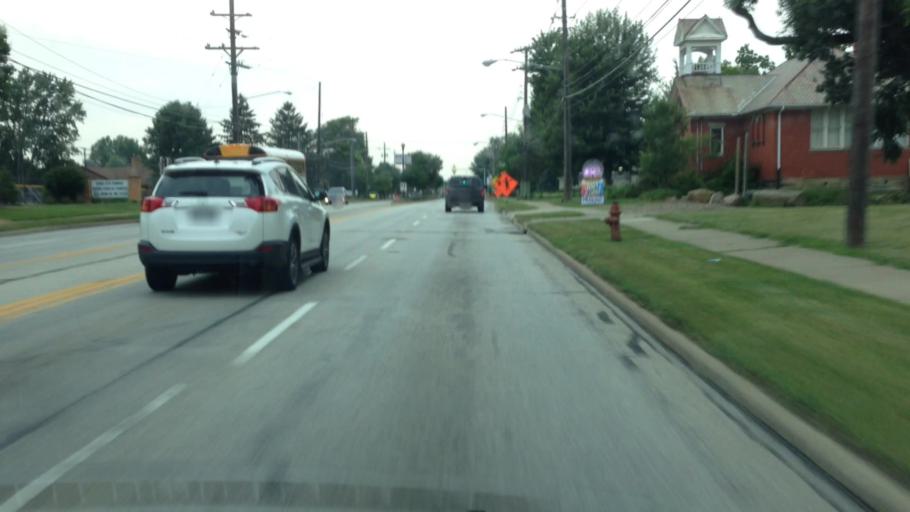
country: US
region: Ohio
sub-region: Cuyahoga County
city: Berea
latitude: 41.3724
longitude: -81.8405
